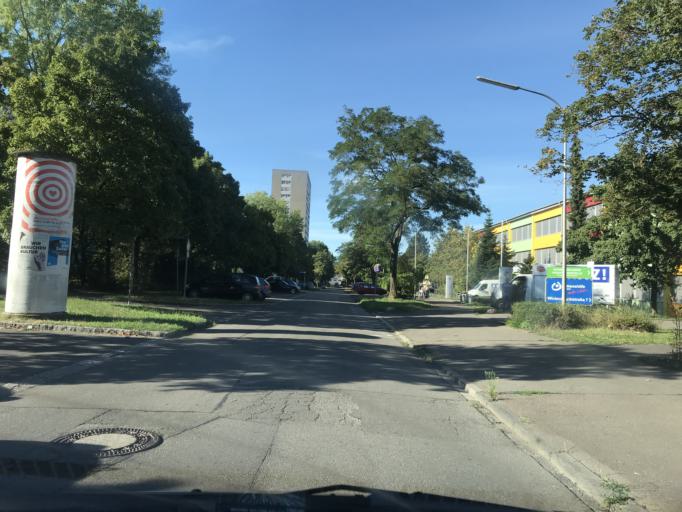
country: DE
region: Baden-Wuerttemberg
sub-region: Freiburg Region
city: Loerrach
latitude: 47.6222
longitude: 7.6632
